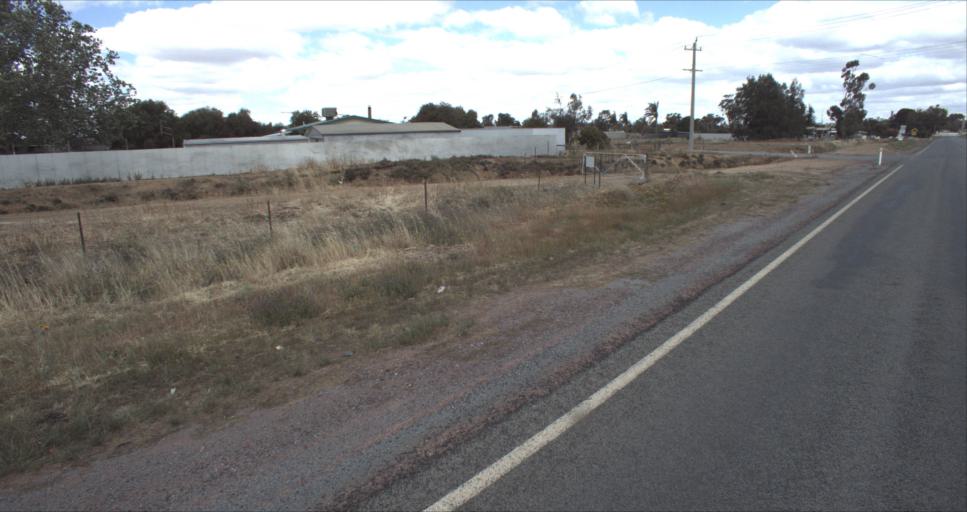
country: AU
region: New South Wales
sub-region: Leeton
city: Leeton
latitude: -34.5951
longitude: 146.4053
